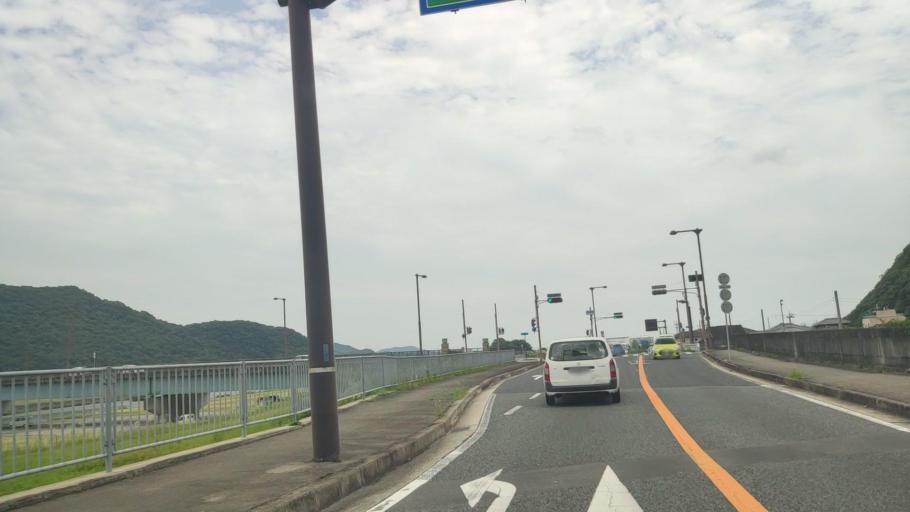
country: JP
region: Hyogo
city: Tatsunocho-tominaga
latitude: 34.8750
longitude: 134.5479
